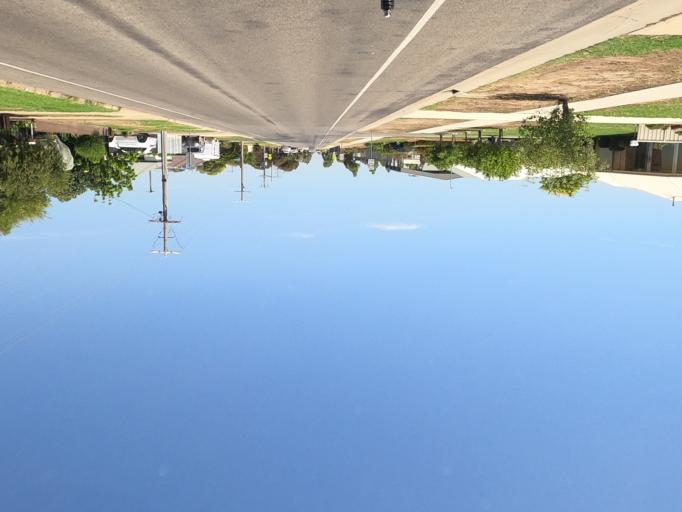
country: AU
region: Victoria
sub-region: Moira
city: Yarrawonga
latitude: -36.0102
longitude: 146.0132
